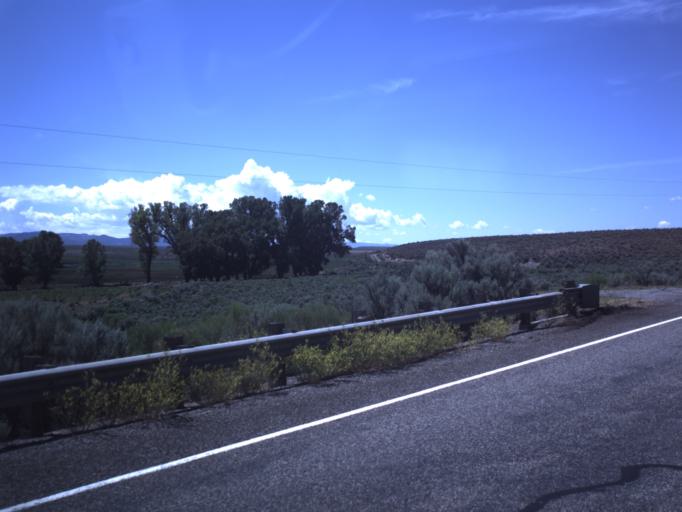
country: US
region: Utah
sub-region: Garfield County
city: Panguitch
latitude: 37.9960
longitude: -112.3884
